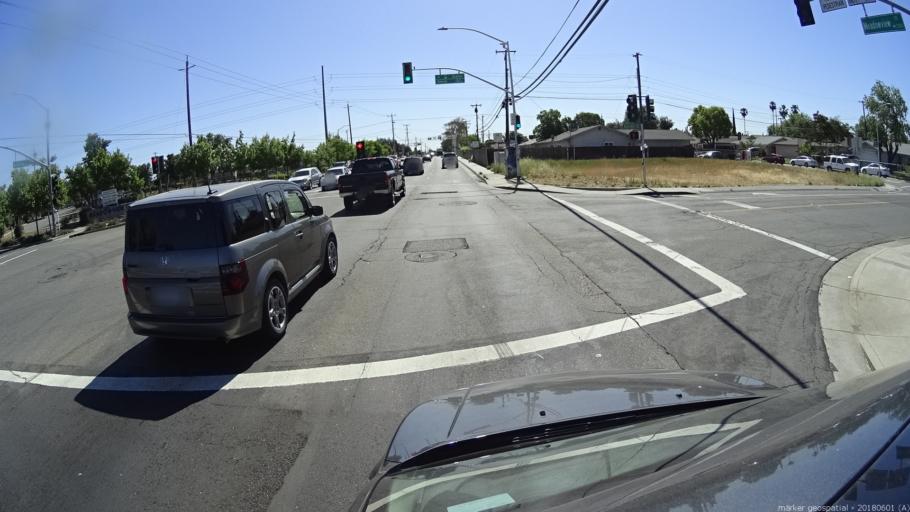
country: US
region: California
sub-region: Sacramento County
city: Parkway
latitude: 38.4815
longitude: -121.4686
